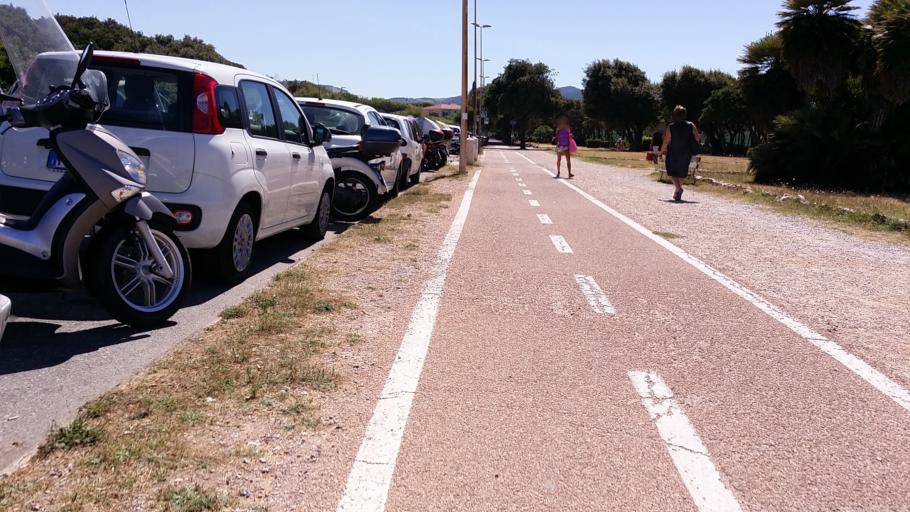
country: IT
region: Tuscany
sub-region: Provincia di Livorno
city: Livorno
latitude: 43.5203
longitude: 10.3132
